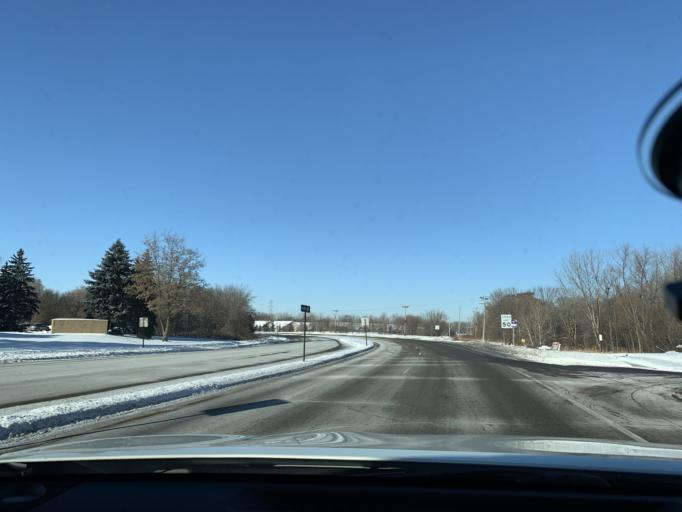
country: US
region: Minnesota
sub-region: Anoka County
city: Coon Rapids
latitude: 45.1453
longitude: -93.2822
